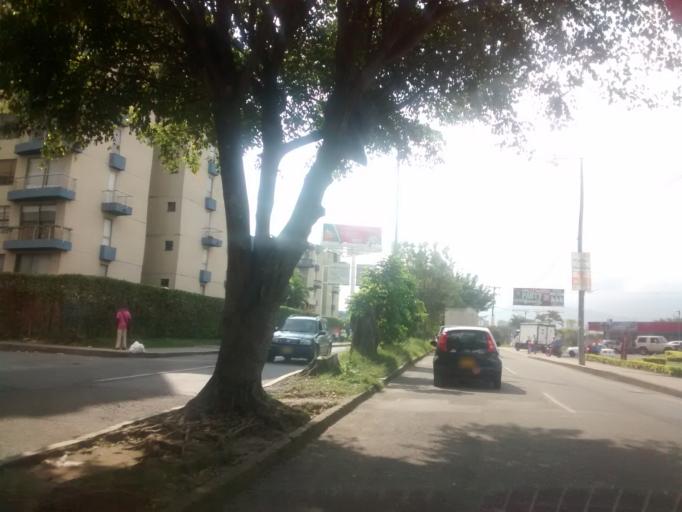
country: CO
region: Tolima
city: Ibague
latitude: 4.4414
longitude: -75.2048
